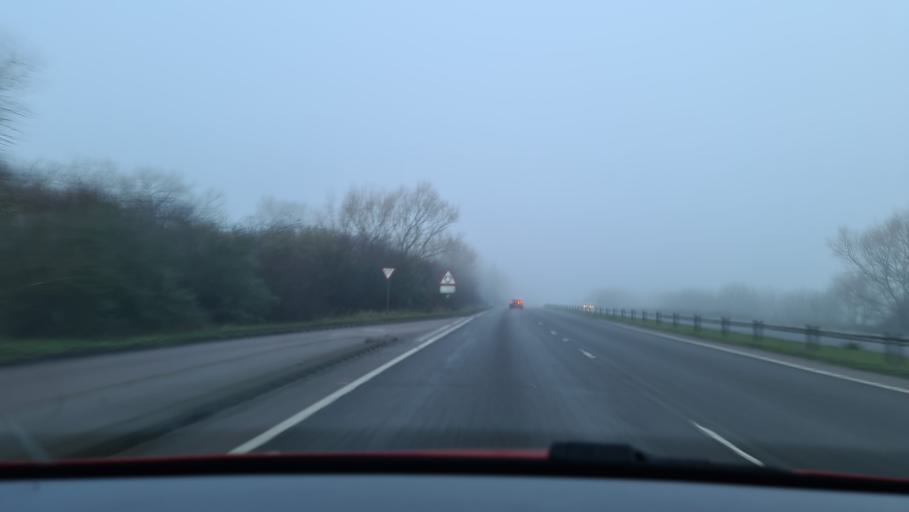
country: GB
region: England
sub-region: Buckinghamshire
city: Aston Clinton
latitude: 51.8078
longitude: -0.7408
